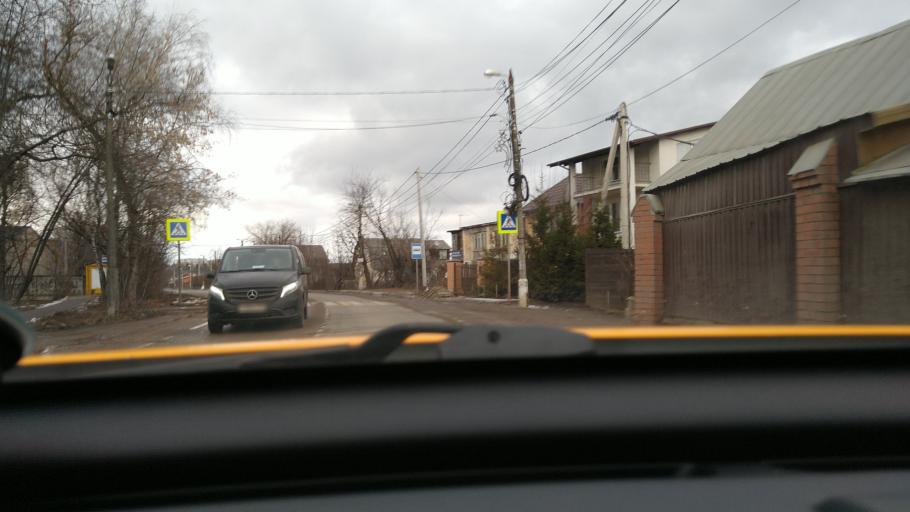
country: RU
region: Moskovskaya
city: Barvikha
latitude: 55.7585
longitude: 37.2331
